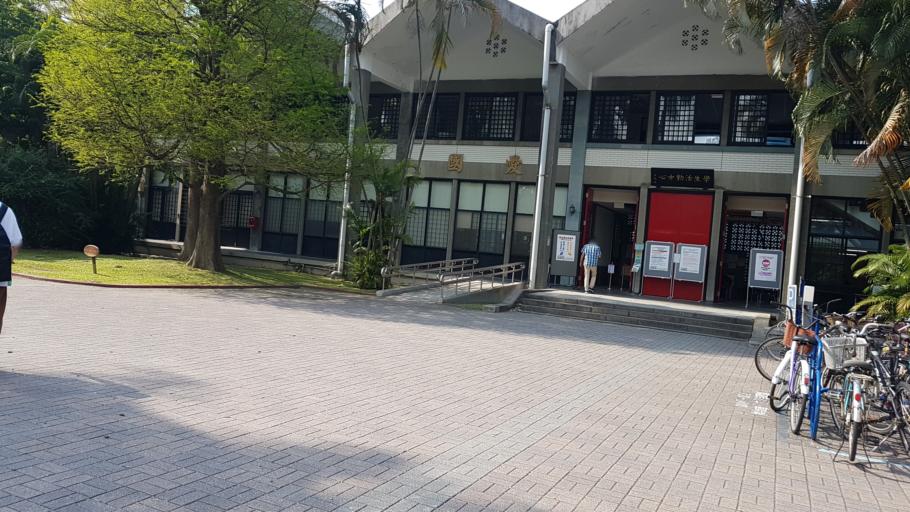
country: TW
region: Taipei
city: Taipei
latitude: 25.0175
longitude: 121.5401
